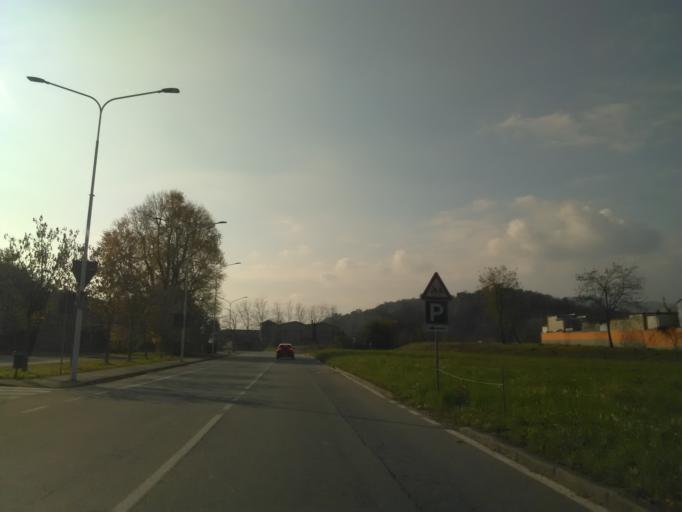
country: IT
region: Piedmont
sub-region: Provincia di Torino
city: Banchette
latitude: 45.4567
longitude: 7.8574
